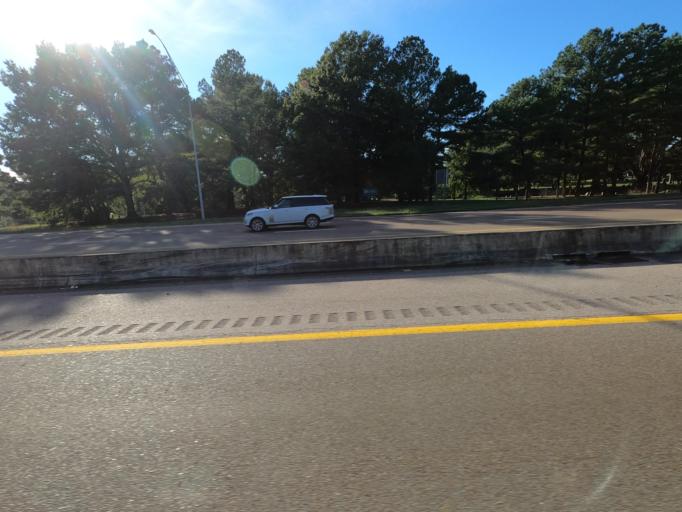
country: US
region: Tennessee
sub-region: Shelby County
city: Memphis
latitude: 35.1206
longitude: -90.0257
